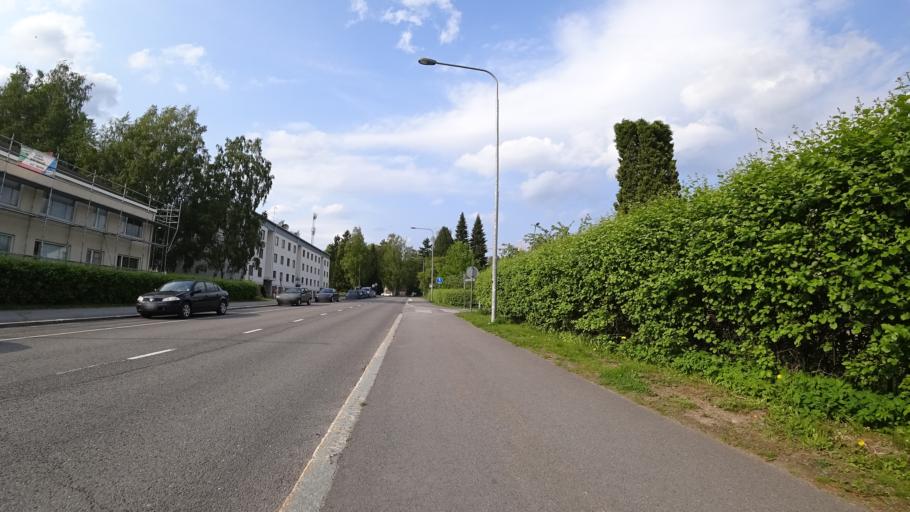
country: FI
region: Pirkanmaa
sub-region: Tampere
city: Pirkkala
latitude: 61.5011
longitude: 23.6290
